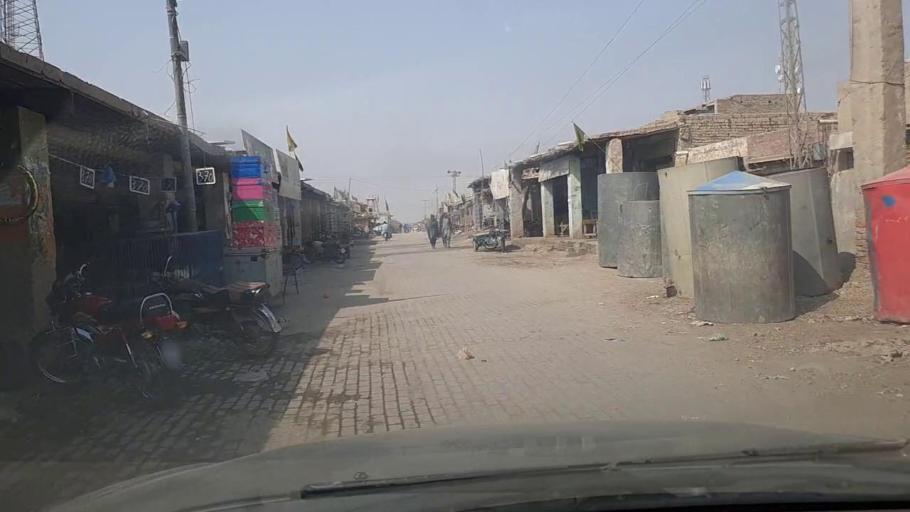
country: PK
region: Sindh
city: Mirpur Mathelo
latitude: 27.9149
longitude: 69.5199
